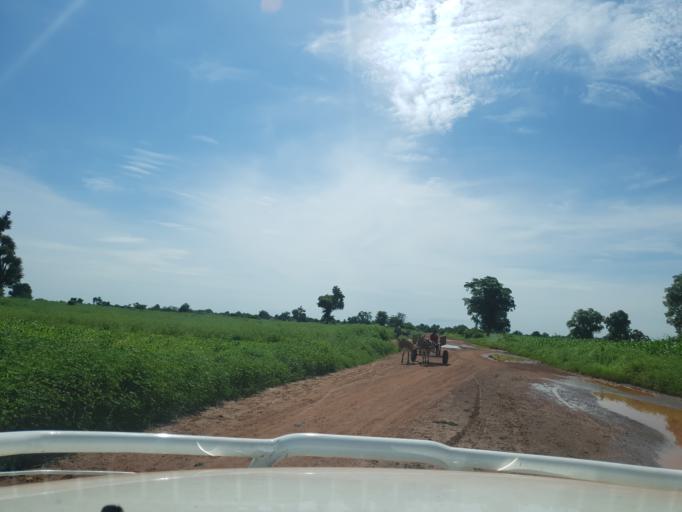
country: ML
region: Koulikoro
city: Banamba
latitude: 13.2760
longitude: -7.5461
